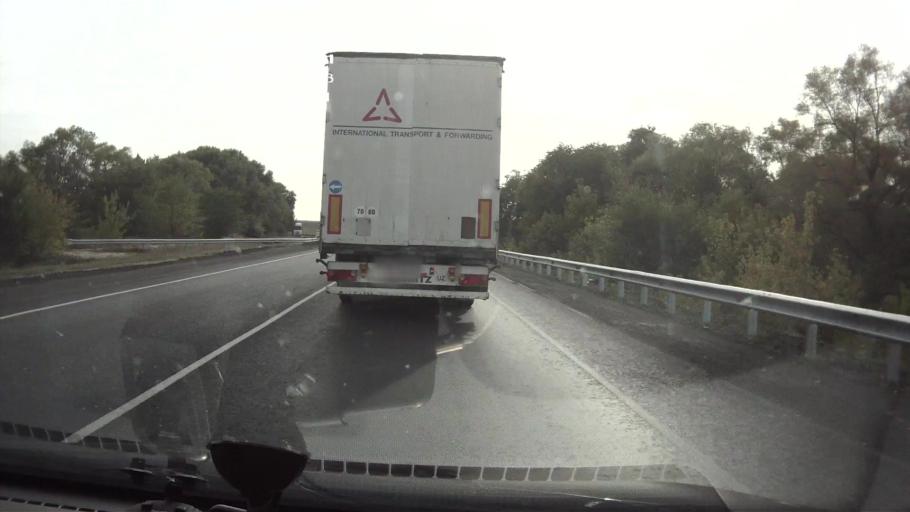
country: RU
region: Saratov
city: Sinodskoye
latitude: 51.9768
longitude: 46.6489
